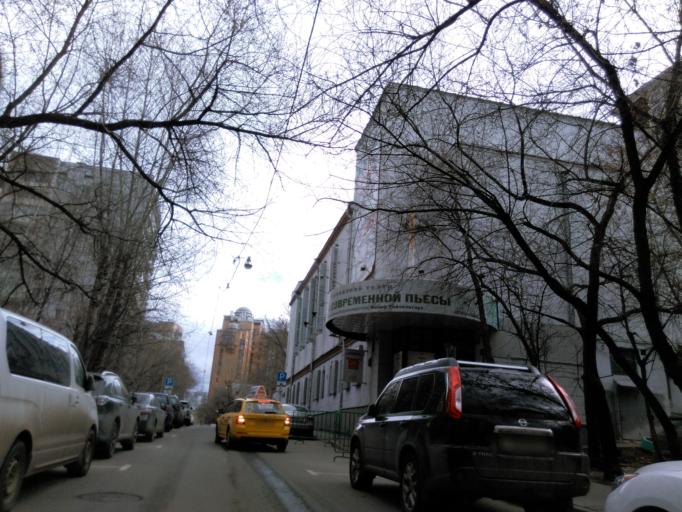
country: RU
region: Moskovskaya
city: Dorogomilovo
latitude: 55.7703
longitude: 37.5762
